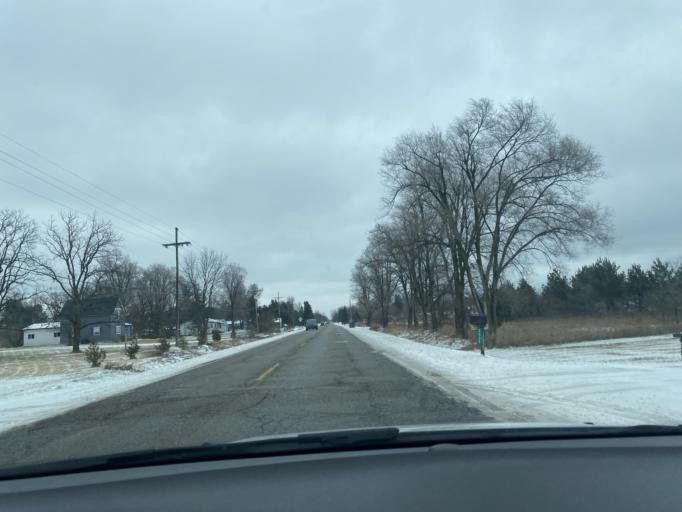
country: US
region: Michigan
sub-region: Lapeer County
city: North Branch
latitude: 43.2065
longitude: -83.2526
